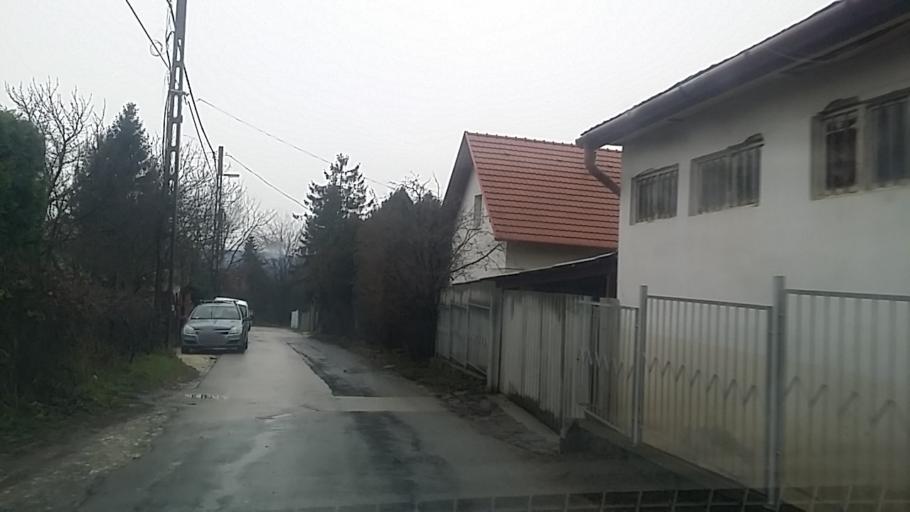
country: HU
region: Pest
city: Budakeszi
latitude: 47.5068
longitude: 18.9305
